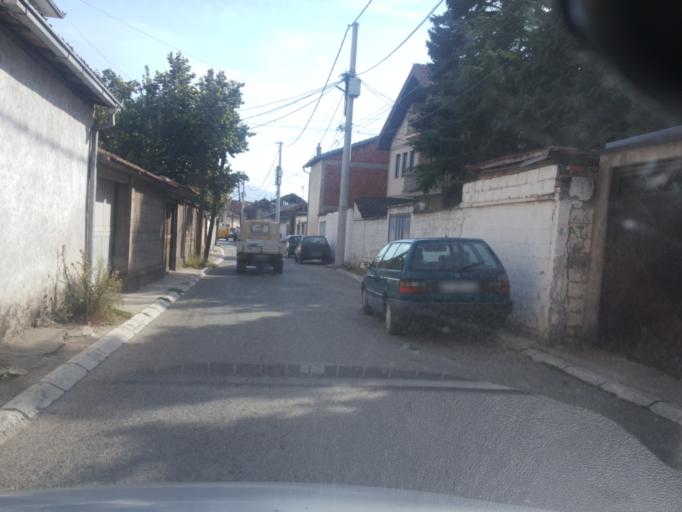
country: XK
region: Gjakova
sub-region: Komuna e Gjakoves
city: Gjakove
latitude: 42.3774
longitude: 20.4252
